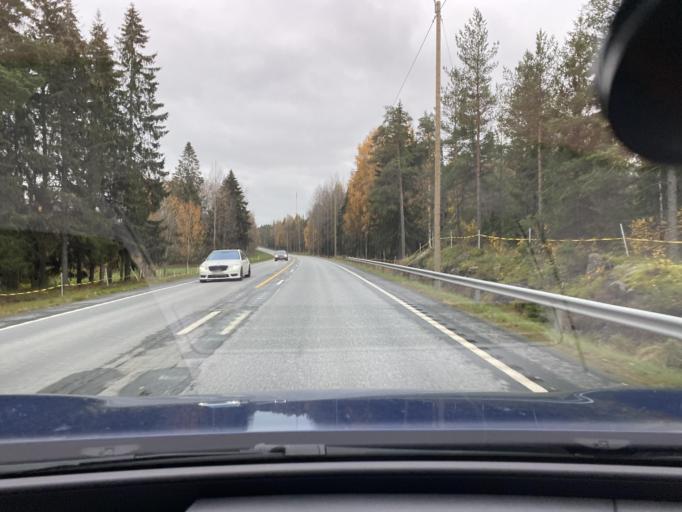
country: FI
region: Varsinais-Suomi
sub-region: Vakka-Suomi
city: Laitila
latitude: 60.9357
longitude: 21.6045
